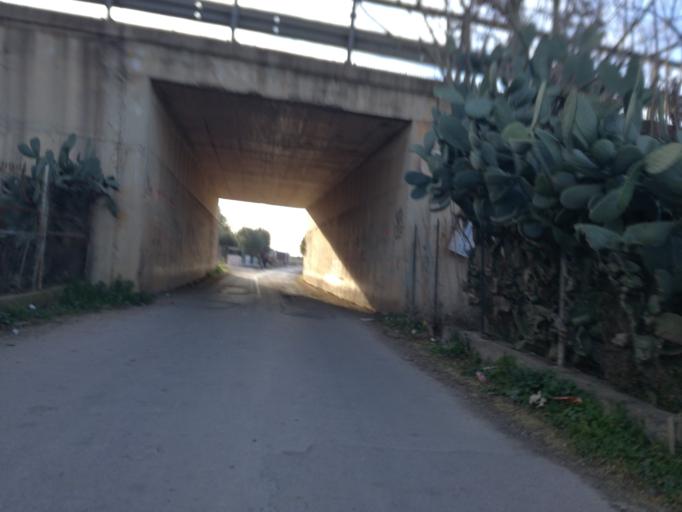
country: IT
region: Apulia
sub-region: Provincia di Bari
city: Capurso
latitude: 41.0494
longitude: 16.9108
